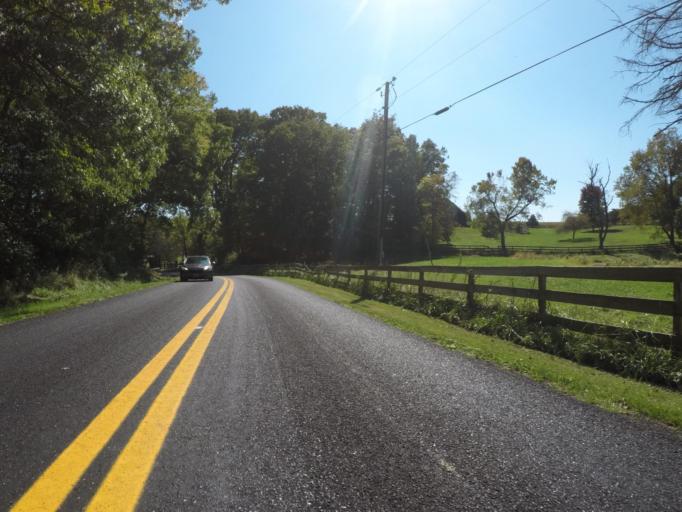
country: US
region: Maryland
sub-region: Carroll County
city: Hampstead
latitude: 39.5875
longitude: -76.8908
